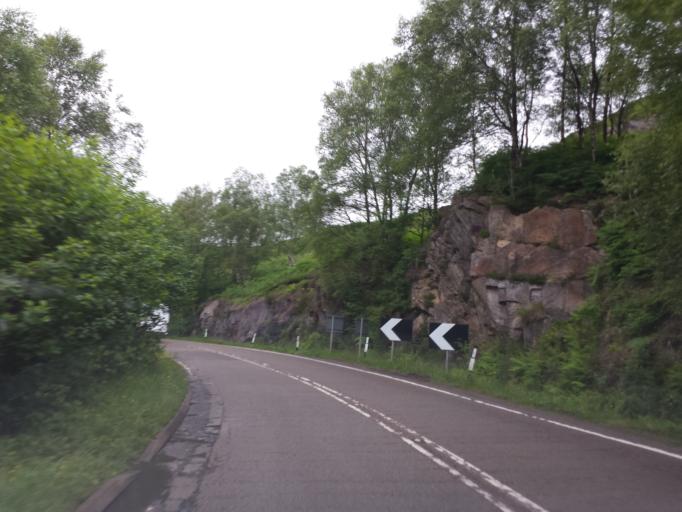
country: GB
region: Scotland
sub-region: Highland
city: Fort William
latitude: 56.8791
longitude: -5.5608
